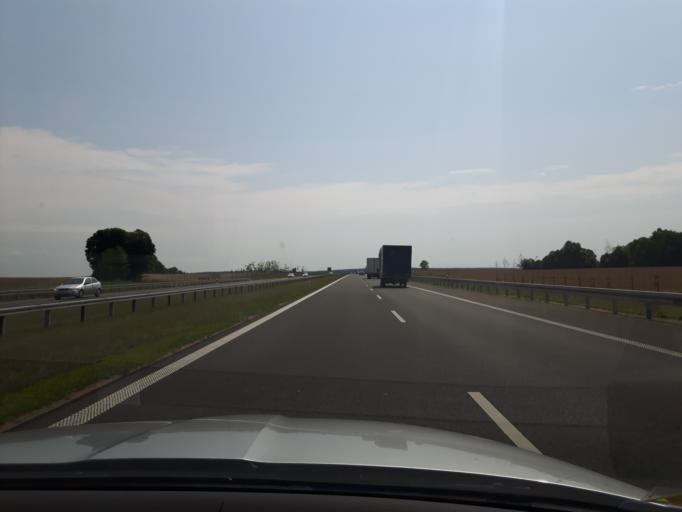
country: PL
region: Warmian-Masurian Voivodeship
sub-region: Powiat nidzicki
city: Nidzica
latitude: 53.2931
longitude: 20.4376
